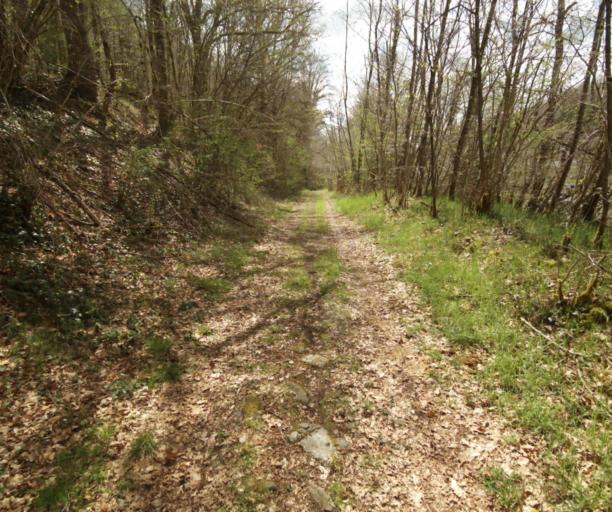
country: FR
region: Limousin
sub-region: Departement de la Correze
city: Argentat
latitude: 45.1791
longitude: 1.8765
